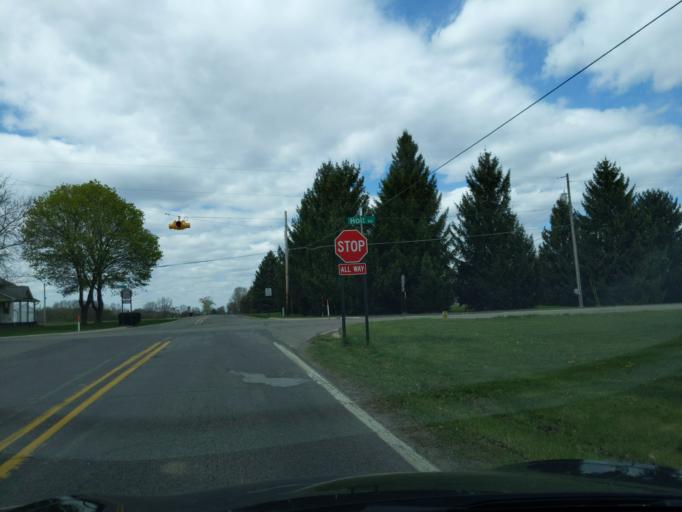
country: US
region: Michigan
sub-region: Ingham County
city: Holt
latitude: 42.6401
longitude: -84.4626
